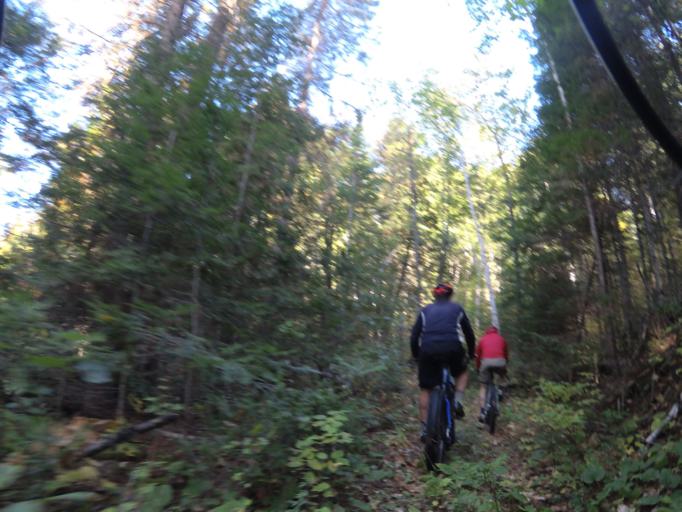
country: CA
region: Ontario
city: Pembroke
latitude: 45.3386
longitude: -77.1675
